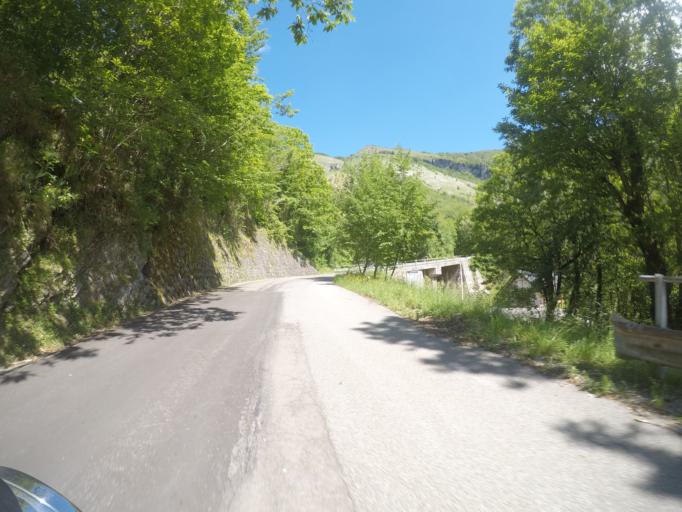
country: IT
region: Tuscany
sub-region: Provincia di Lucca
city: Fontana delle Monache
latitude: 44.0650
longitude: 10.3086
